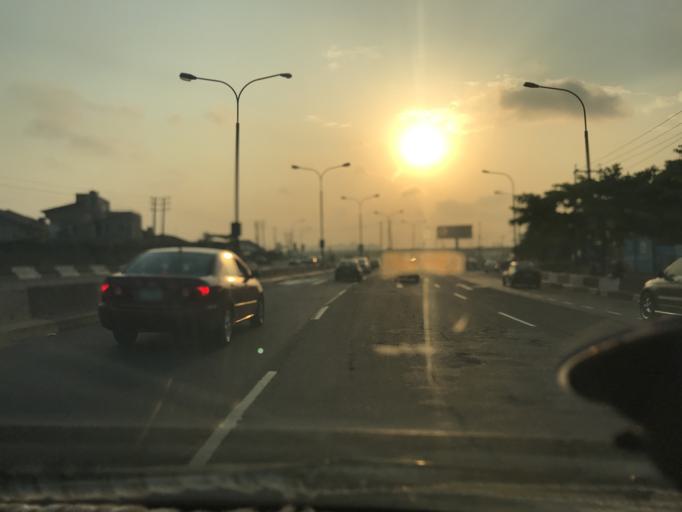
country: NG
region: Lagos
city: Lagos
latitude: 6.4582
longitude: 3.4052
